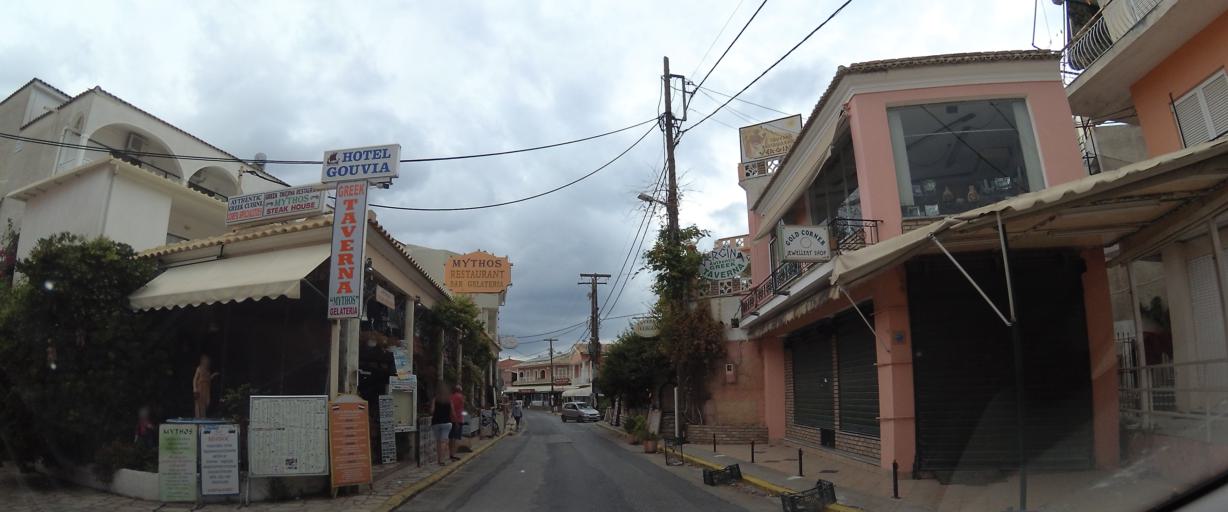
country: GR
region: Ionian Islands
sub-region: Nomos Kerkyras
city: Kontokali
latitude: 39.6521
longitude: 19.8448
